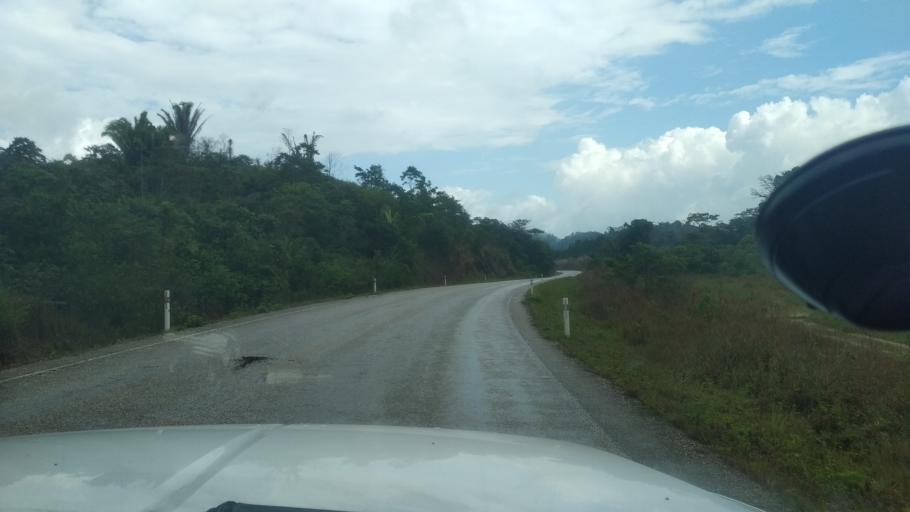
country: GT
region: Peten
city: San Luis
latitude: 16.1898
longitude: -89.1856
